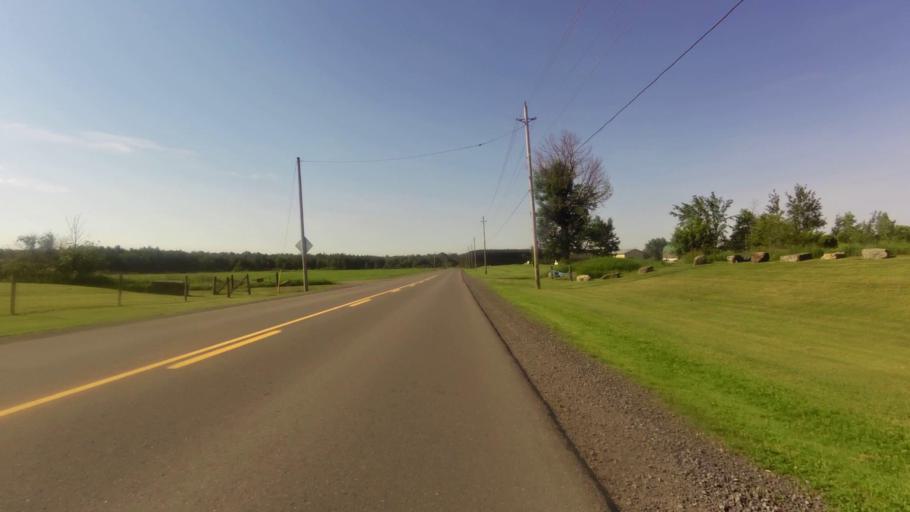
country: CA
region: Ontario
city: Ottawa
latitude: 45.2288
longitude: -75.5609
